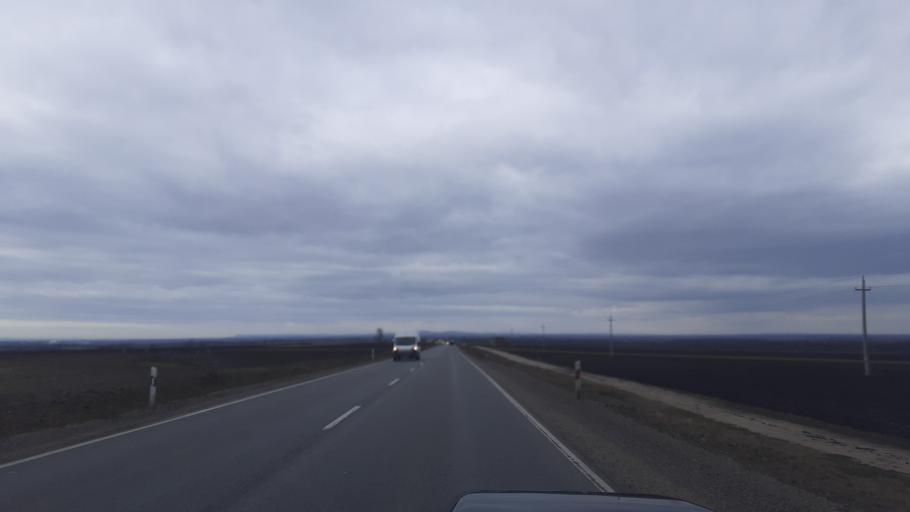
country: HU
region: Fejer
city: Perkata
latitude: 47.0497
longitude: 18.8153
